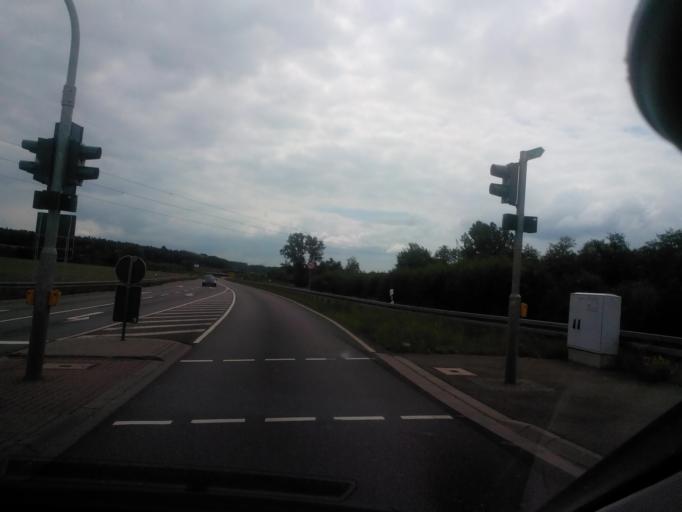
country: DE
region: Saarland
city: Uberherrn
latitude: 49.2496
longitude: 6.7171
